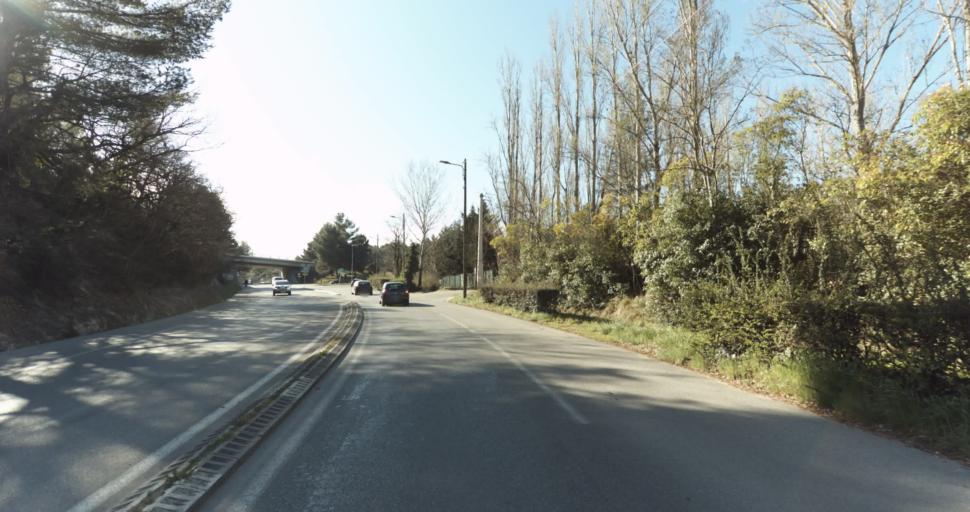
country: FR
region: Provence-Alpes-Cote d'Azur
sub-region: Departement des Bouches-du-Rhone
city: Aix-en-Provence
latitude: 43.5541
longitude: 5.4342
